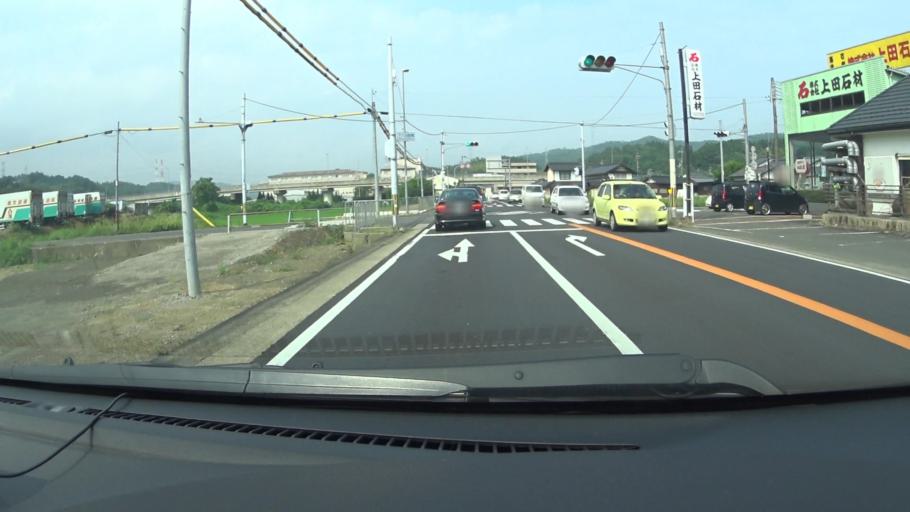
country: JP
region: Kyoto
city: Ayabe
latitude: 35.3108
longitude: 135.2787
